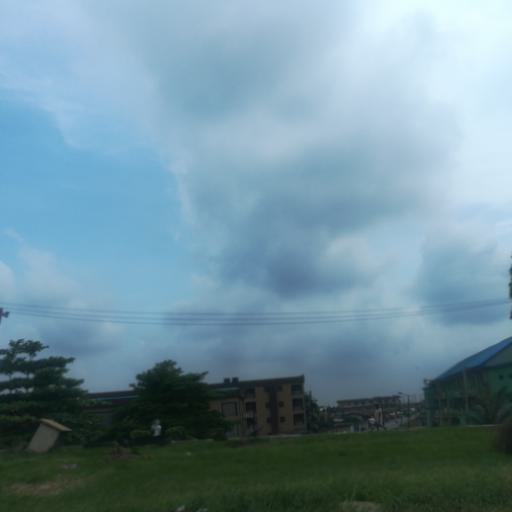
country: NG
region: Lagos
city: Ojota
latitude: 6.5897
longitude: 3.3859
